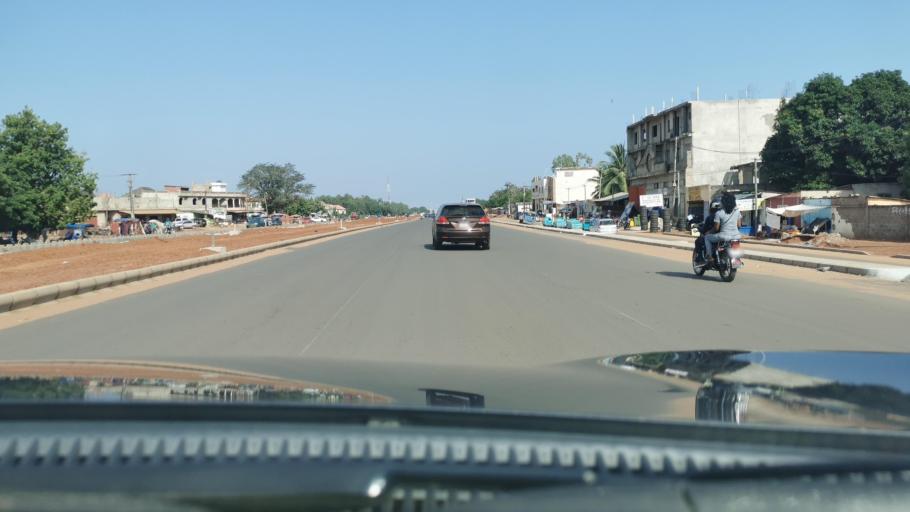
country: TG
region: Maritime
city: Lome
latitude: 6.1950
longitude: 1.1552
